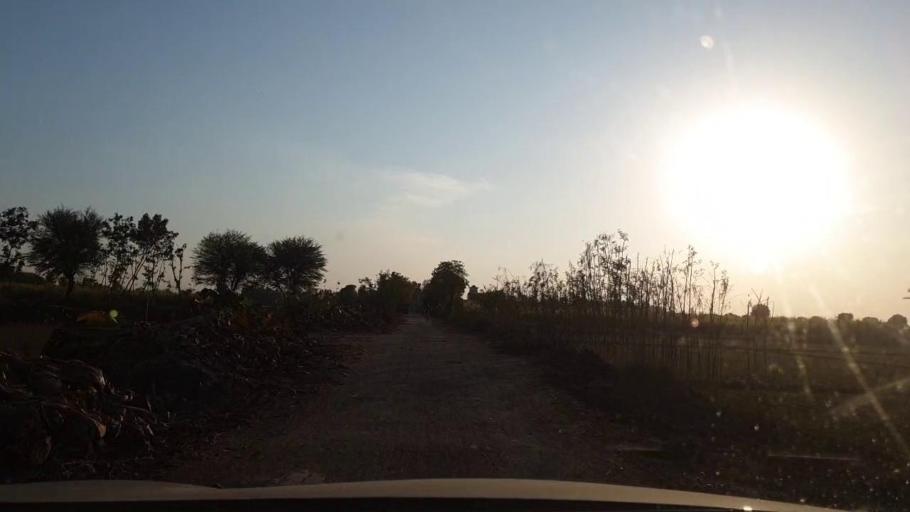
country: PK
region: Sindh
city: Tando Adam
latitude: 25.6155
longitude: 68.6795
